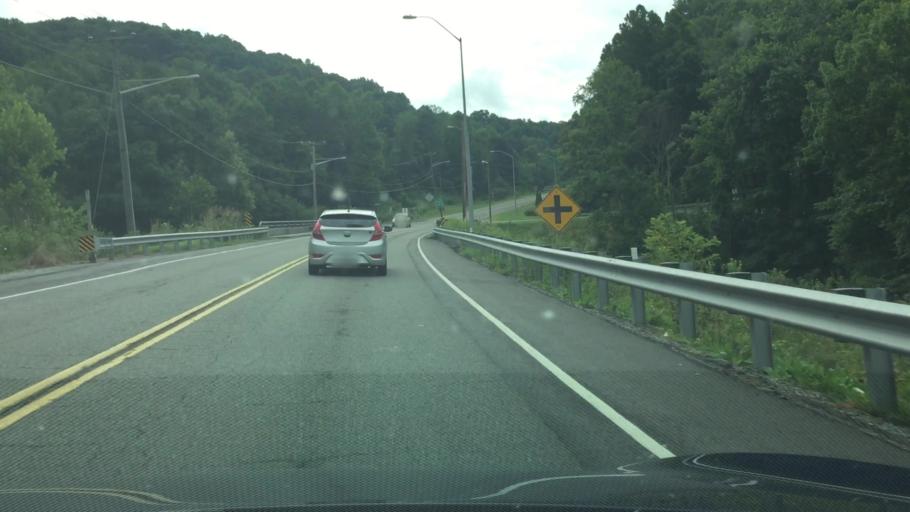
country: US
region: Virginia
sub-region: Pulaski County
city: Pulaski
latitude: 37.0422
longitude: -80.7421
